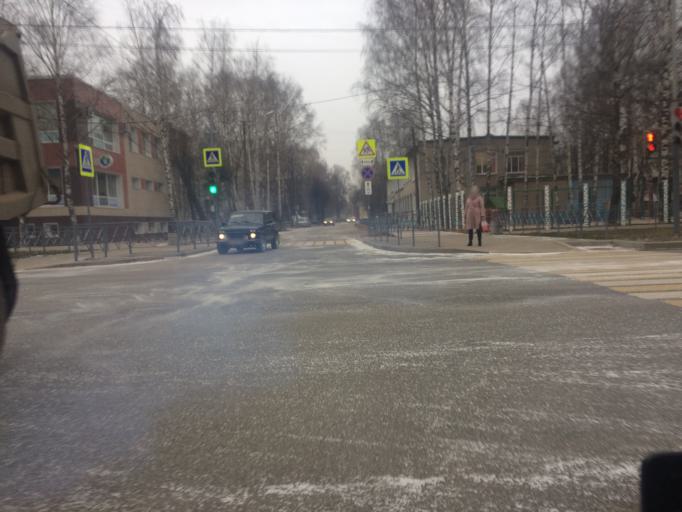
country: RU
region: Mariy-El
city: Yoshkar-Ola
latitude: 56.6424
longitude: 47.8979
